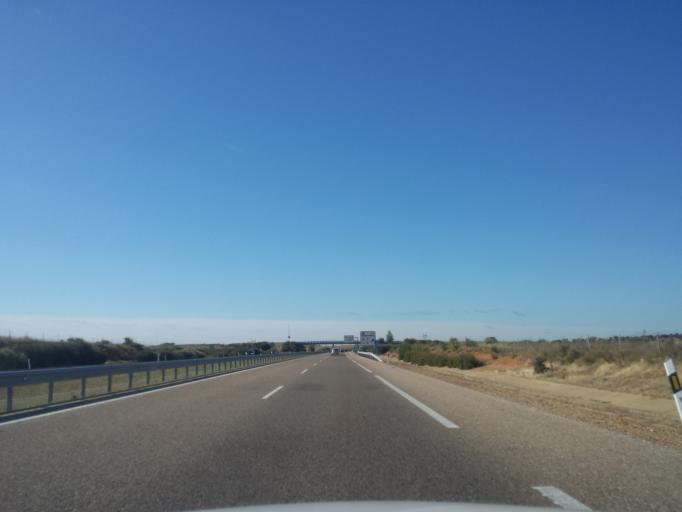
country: ES
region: Castille and Leon
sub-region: Provincia de Leon
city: Villaquejida
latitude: 42.1606
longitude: -5.6359
